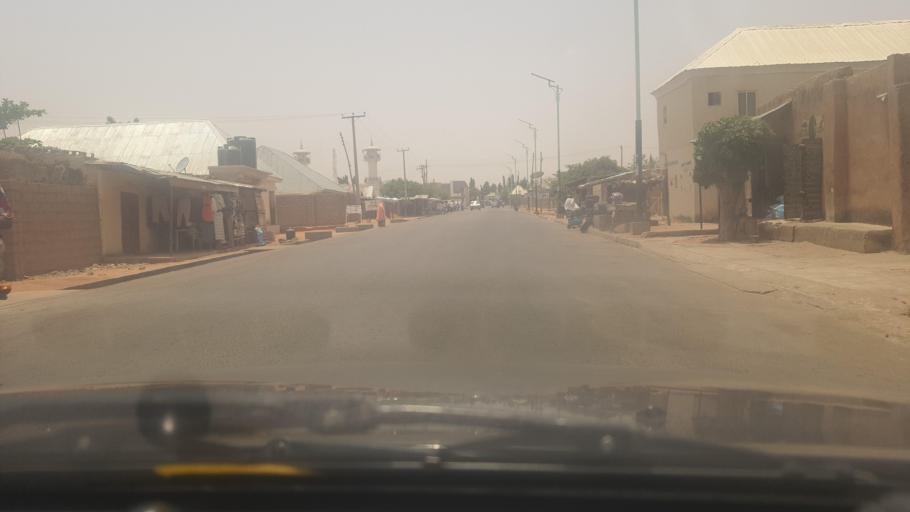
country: NG
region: Gombe
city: Gombe
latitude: 10.2989
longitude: 11.1499
